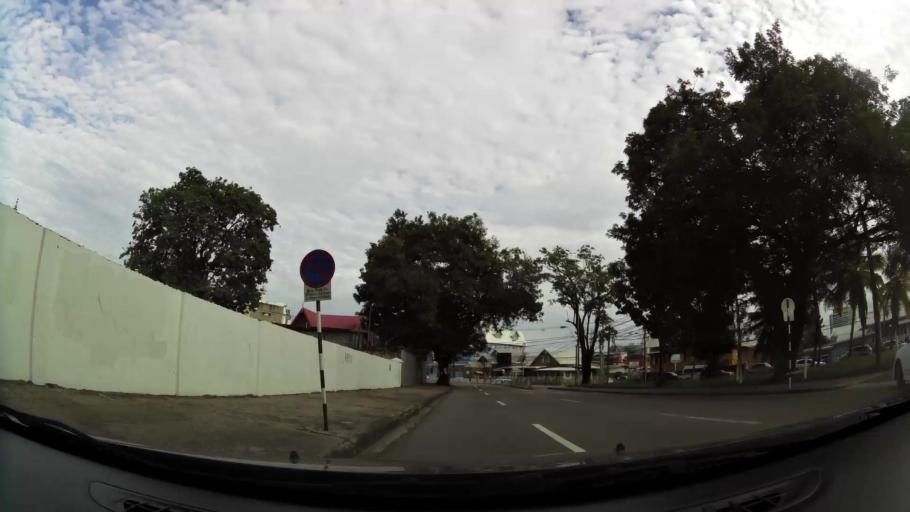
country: TT
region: City of Port of Spain
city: Port-of-Spain
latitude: 10.6570
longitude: -61.5170
